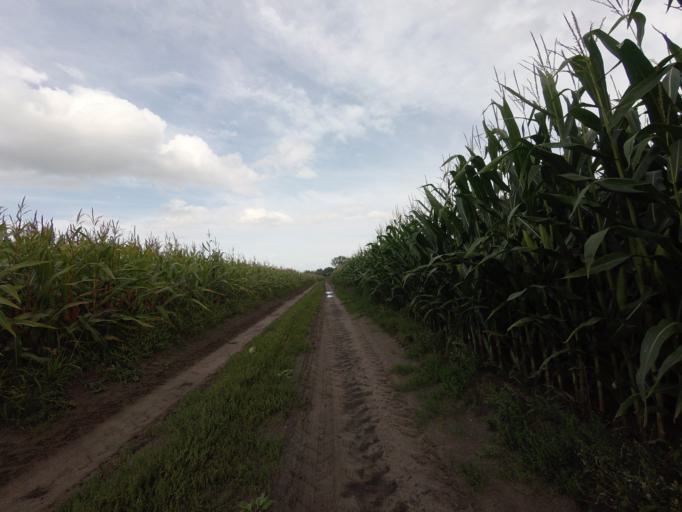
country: BE
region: Flanders
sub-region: Provincie Vlaams-Brabant
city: Kapelle-op-den-Bos
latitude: 51.0193
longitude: 4.3796
